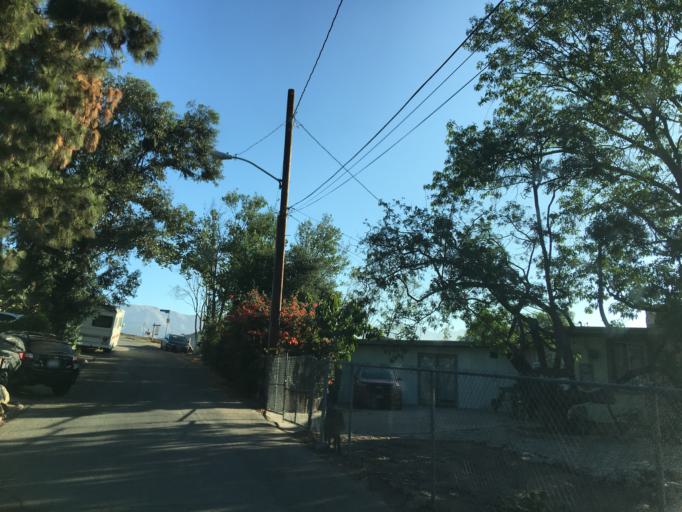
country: US
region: California
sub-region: Los Angeles County
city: San Fernando
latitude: 34.2868
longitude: -118.3769
